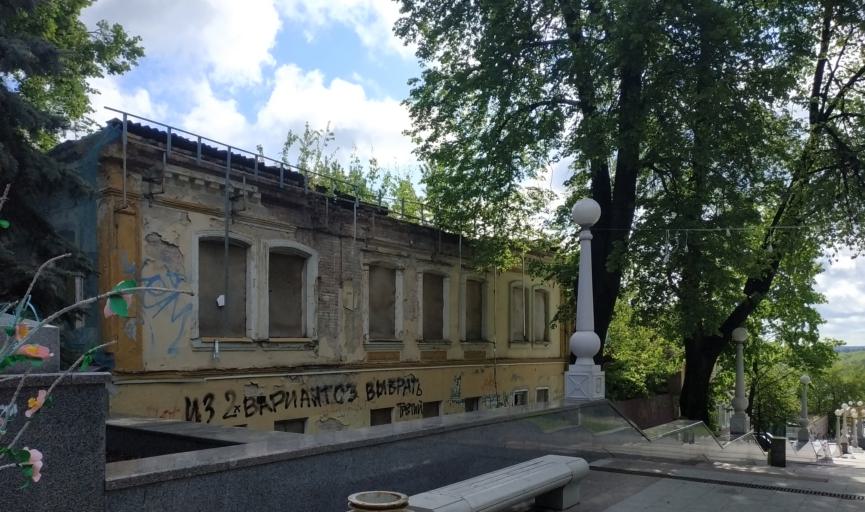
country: RU
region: Brjansk
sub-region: Bryanskiy Rayon
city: Bryansk
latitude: 53.2414
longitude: 34.3688
